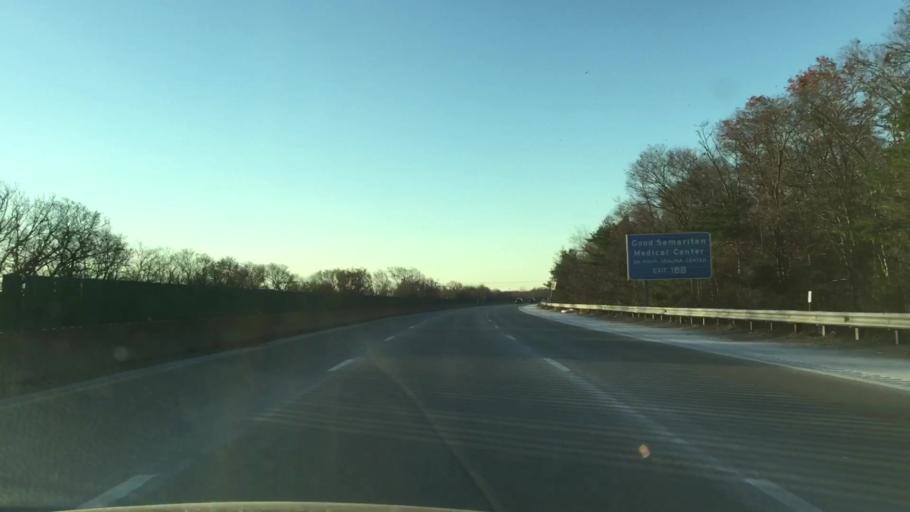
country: US
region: Massachusetts
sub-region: Norfolk County
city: Avon
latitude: 42.1040
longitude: -71.0579
